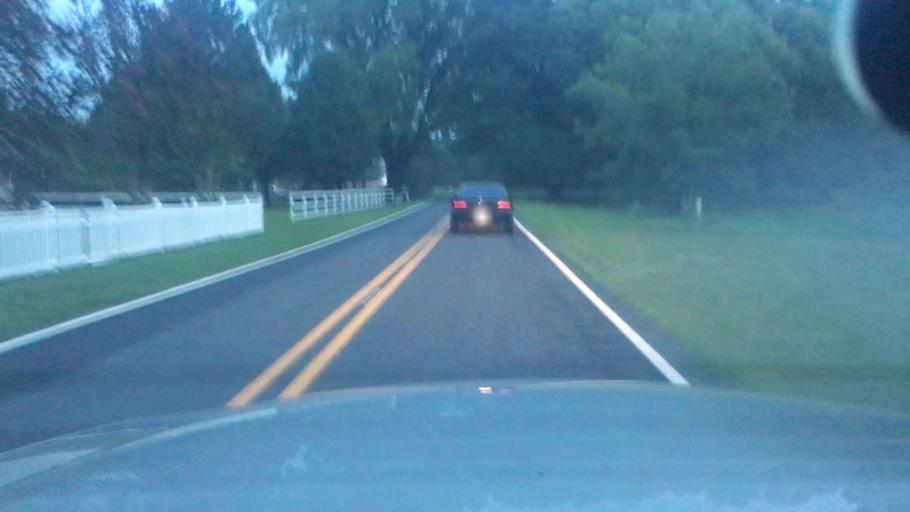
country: US
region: North Carolina
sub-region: Cumberland County
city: Hope Mills
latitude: 34.9651
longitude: -78.9271
